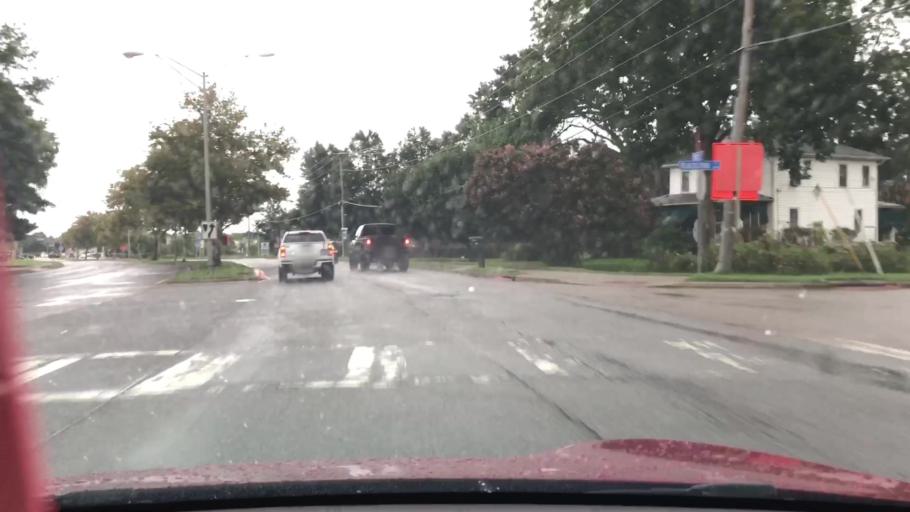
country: US
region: Virginia
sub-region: City of Chesapeake
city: Chesapeake
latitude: 36.8442
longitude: -76.1902
